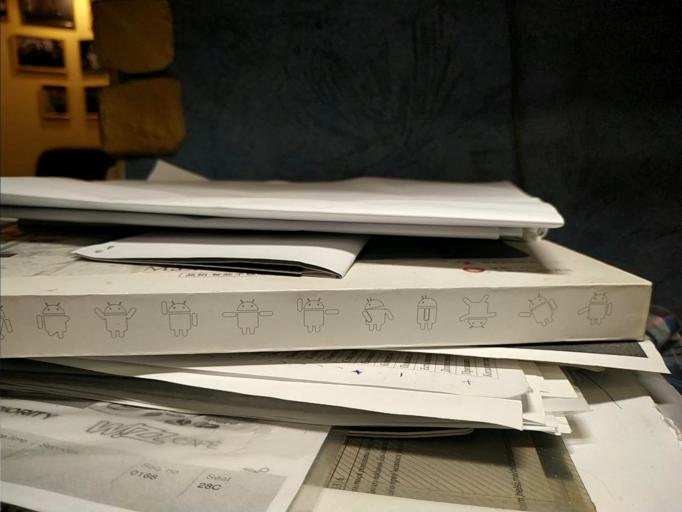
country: RU
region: Tverskaya
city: Zubtsov
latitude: 56.0830
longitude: 34.7862
